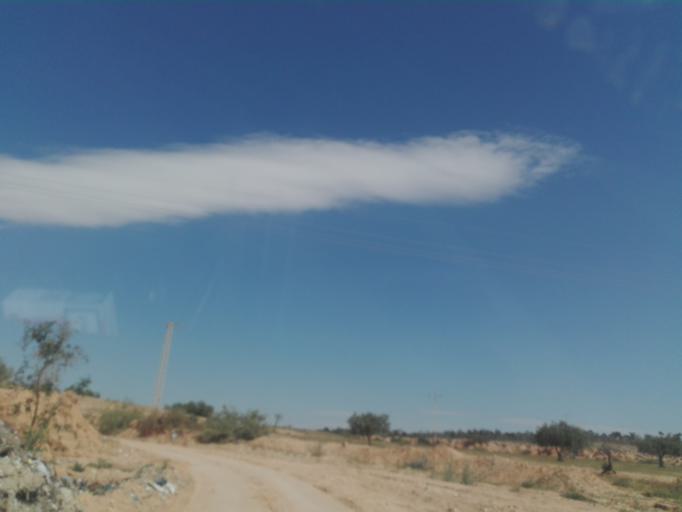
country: TN
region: Safaqis
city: Sfax
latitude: 34.6866
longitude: 10.5596
